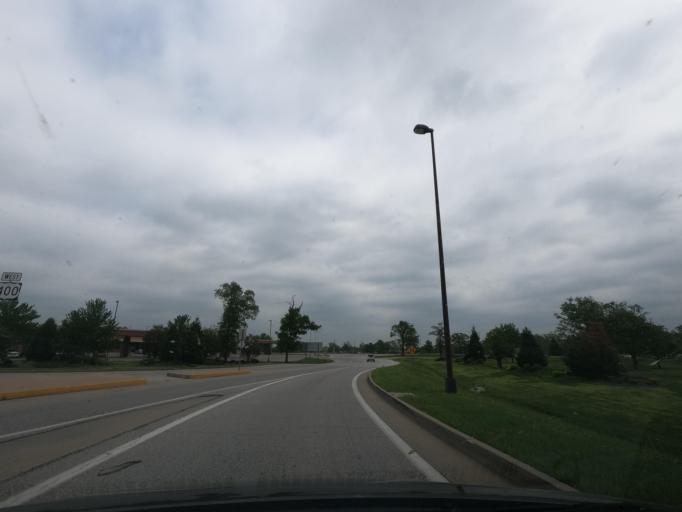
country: US
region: Kansas
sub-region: Cherokee County
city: Galena
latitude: 37.0021
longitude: -94.6151
